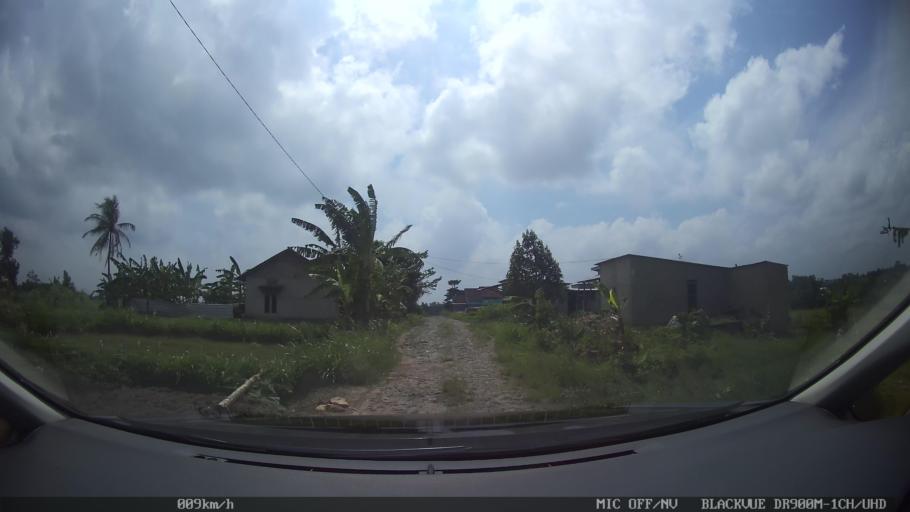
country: ID
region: Lampung
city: Kedaton
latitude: -5.3313
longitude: 105.2969
